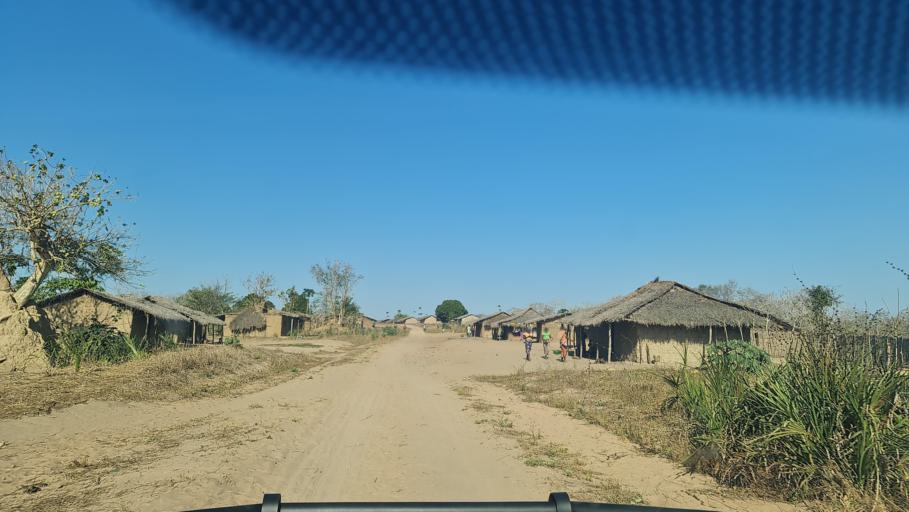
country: MZ
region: Nampula
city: Nacala
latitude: -13.9407
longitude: 40.4876
